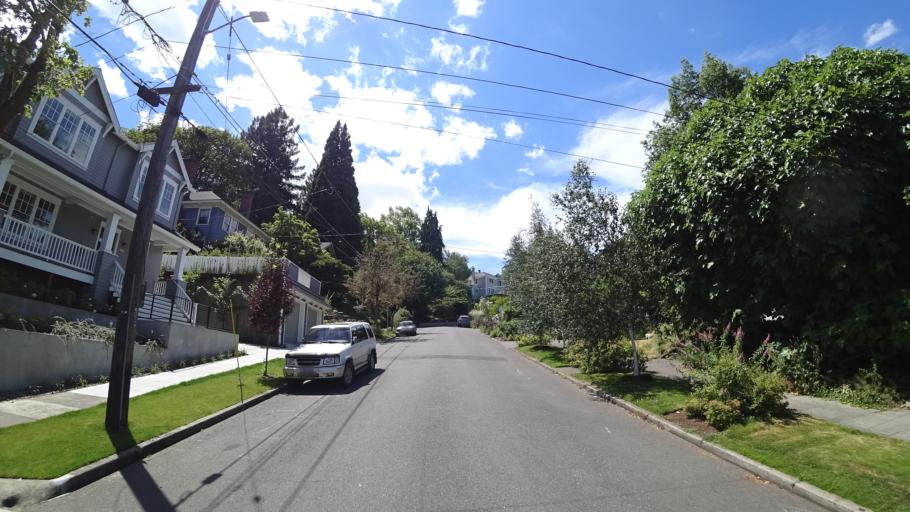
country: US
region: Oregon
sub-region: Multnomah County
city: Portland
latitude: 45.5318
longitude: -122.7058
